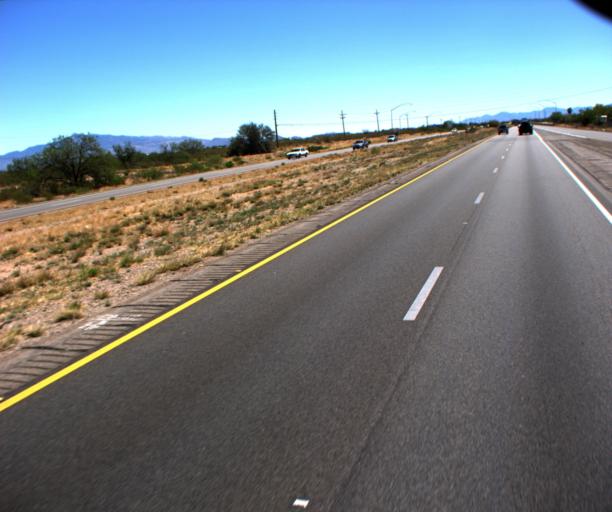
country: US
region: Arizona
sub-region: Pima County
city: Summit
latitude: 32.1019
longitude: -110.8382
